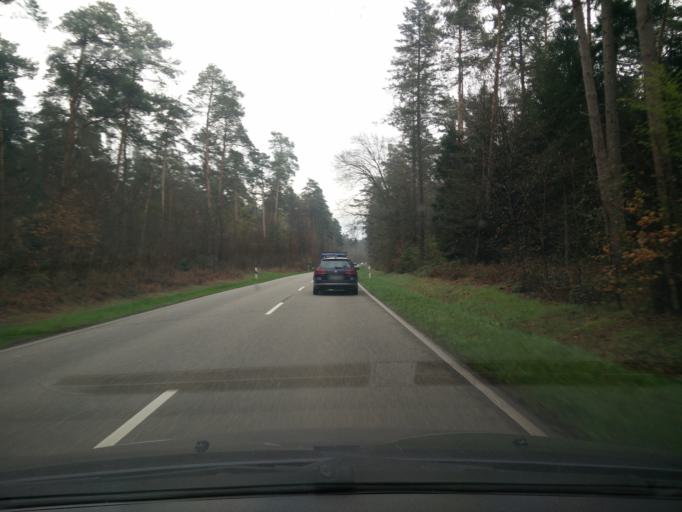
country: DE
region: Rheinland-Pfalz
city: Freckenfeld
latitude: 49.0484
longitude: 8.1132
